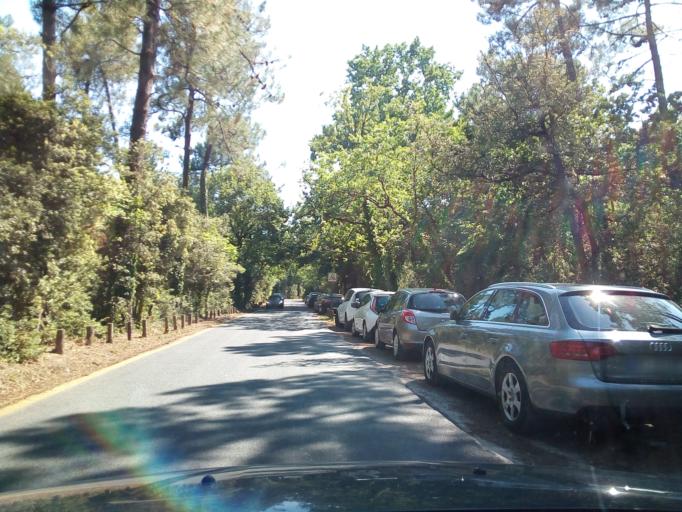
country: FR
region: Poitou-Charentes
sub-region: Departement de la Charente-Maritime
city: Boyard-Ville
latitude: 45.9836
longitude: -1.2945
